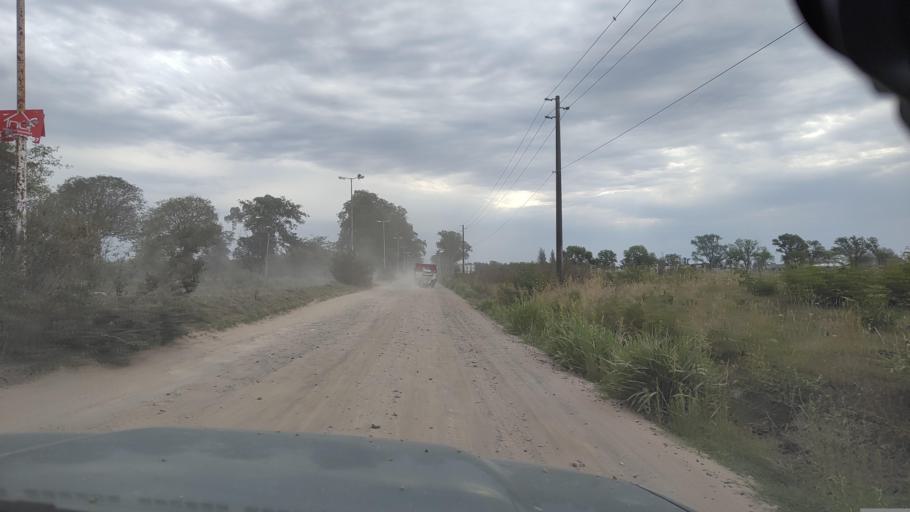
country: AR
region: Buenos Aires
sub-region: Partido de Lujan
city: Lujan
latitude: -34.5491
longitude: -59.0851
